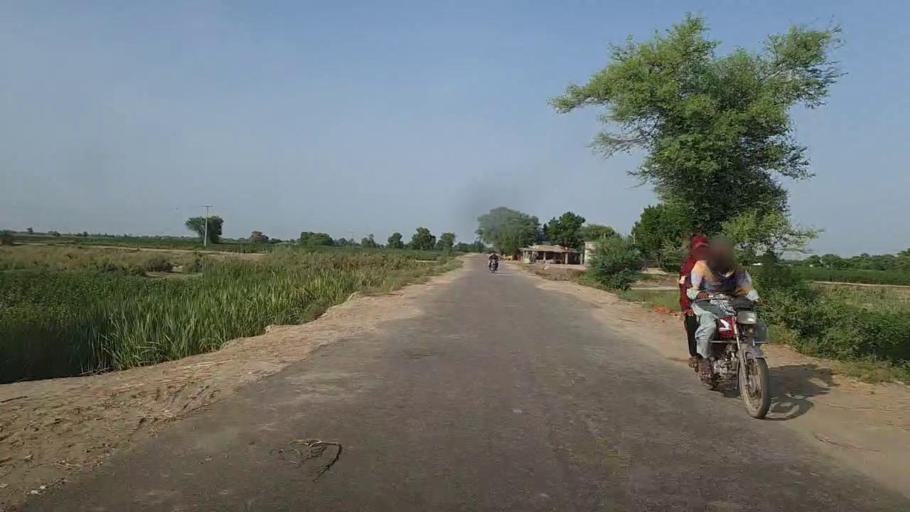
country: PK
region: Sindh
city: Khairpur
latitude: 28.0789
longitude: 69.8326
